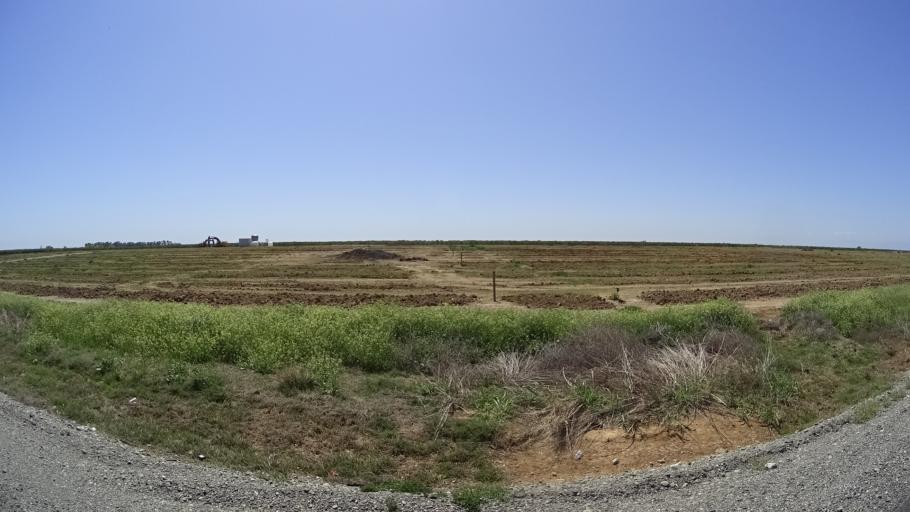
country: US
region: California
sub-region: Glenn County
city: Hamilton City
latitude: 39.7665
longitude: -122.0611
